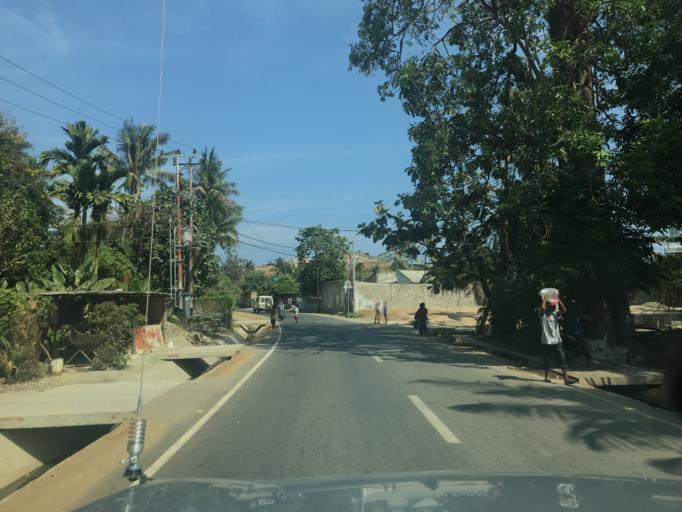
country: TL
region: Dili
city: Dili
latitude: -8.5553
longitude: 125.5185
